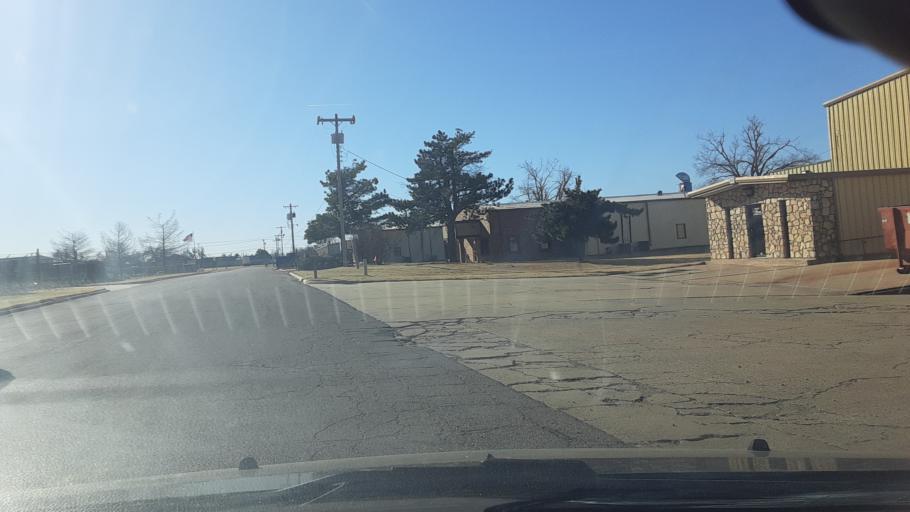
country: US
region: Oklahoma
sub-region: Logan County
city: Guthrie
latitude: 35.8587
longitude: -97.4276
